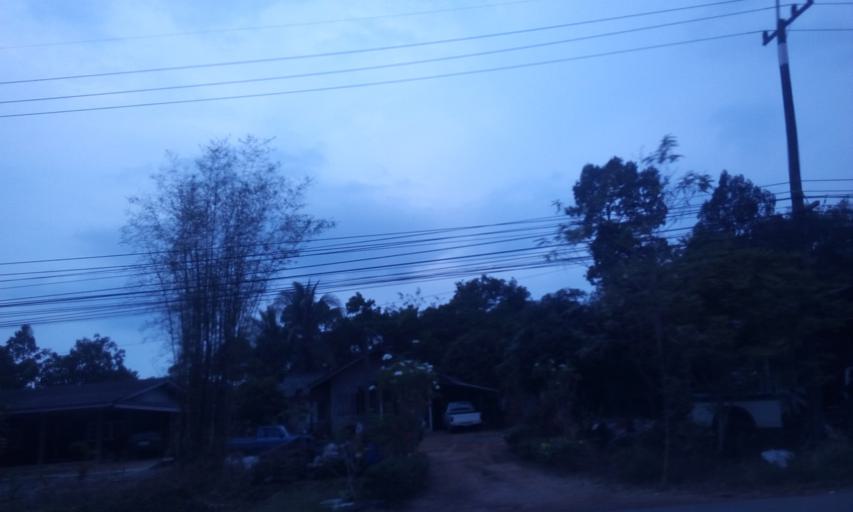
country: TH
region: Chanthaburi
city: Khlung
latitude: 12.4166
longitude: 102.3273
